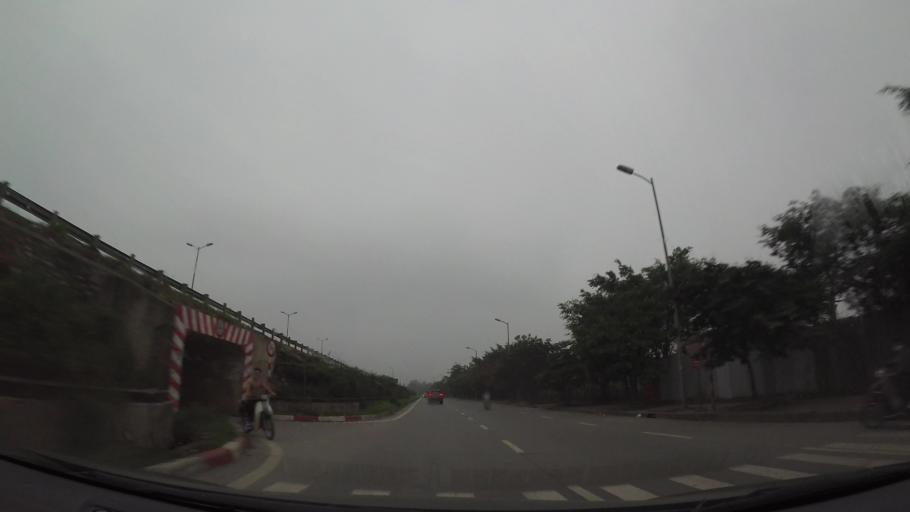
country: VN
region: Ha Noi
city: Van Dien
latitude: 20.9759
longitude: 105.8862
